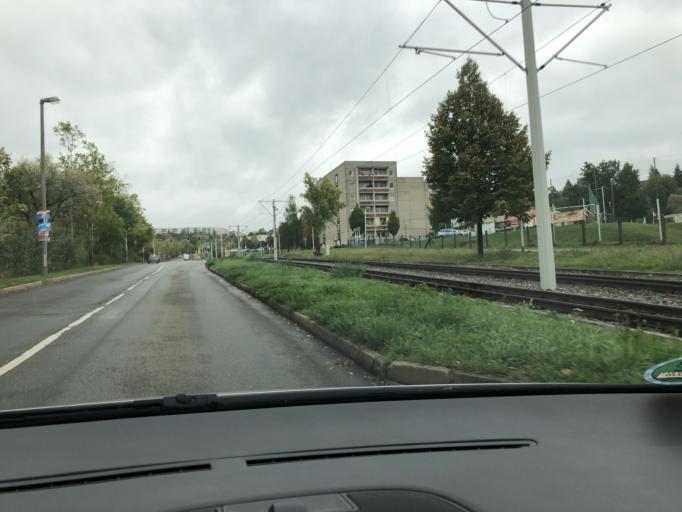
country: DE
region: Thuringia
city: Gera
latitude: 50.9051
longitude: 12.0832
